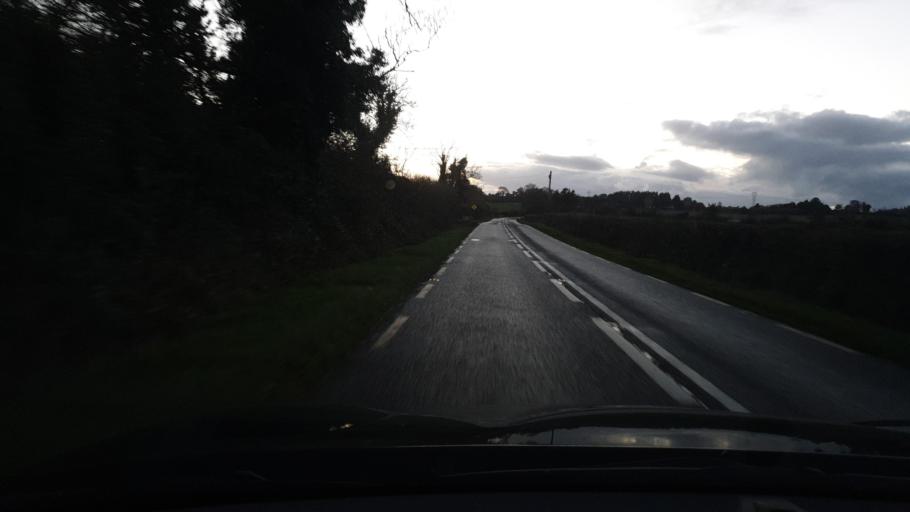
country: IE
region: Leinster
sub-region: An Mhi
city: Slane
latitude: 53.7094
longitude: -6.5041
